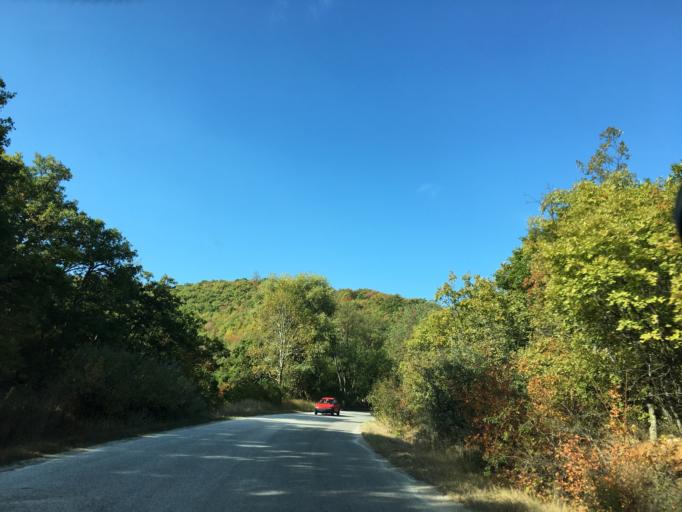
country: BG
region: Khaskovo
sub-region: Obshtina Ivaylovgrad
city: Ivaylovgrad
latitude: 41.5366
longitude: 26.0855
